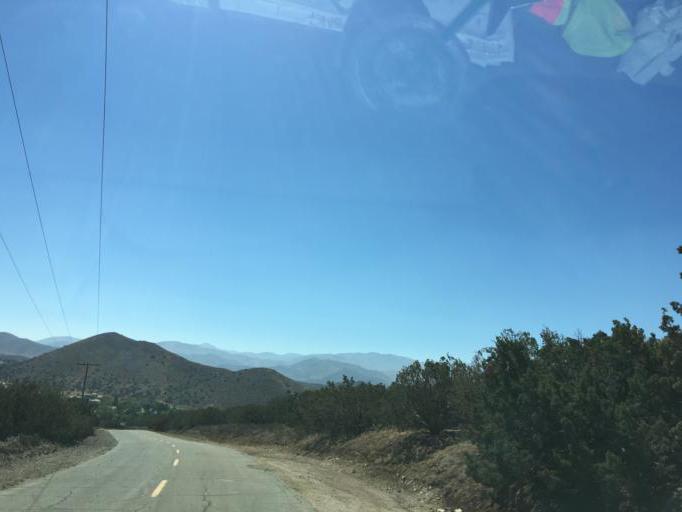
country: US
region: California
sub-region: Los Angeles County
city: Acton
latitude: 34.5071
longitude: -118.2028
